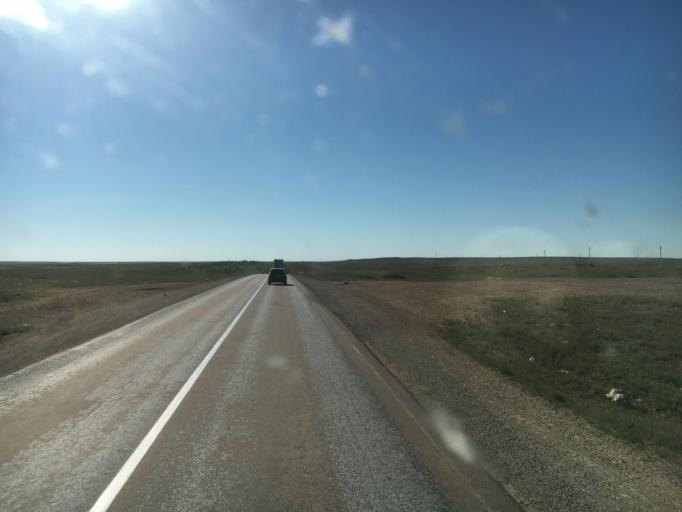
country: RU
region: Orenburg
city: Dombarovskiy
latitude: 50.0817
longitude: 59.5694
